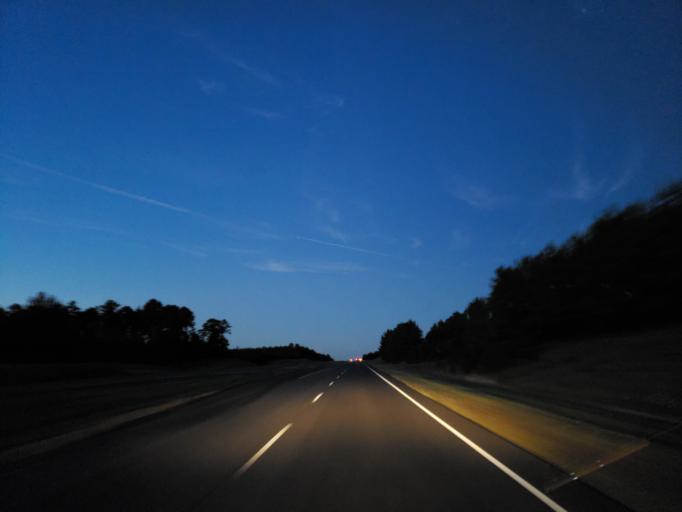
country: US
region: Mississippi
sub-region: Clarke County
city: Quitman
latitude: 32.0166
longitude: -88.6865
